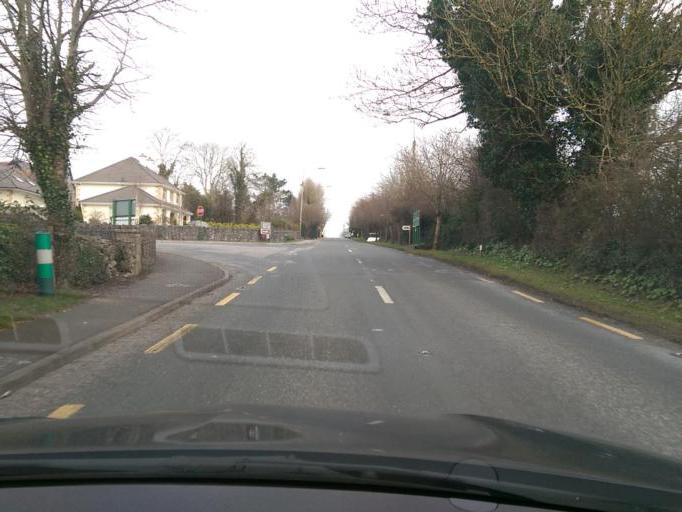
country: IE
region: Connaught
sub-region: Roscommon
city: Roscommon
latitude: 53.5199
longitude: -8.3343
